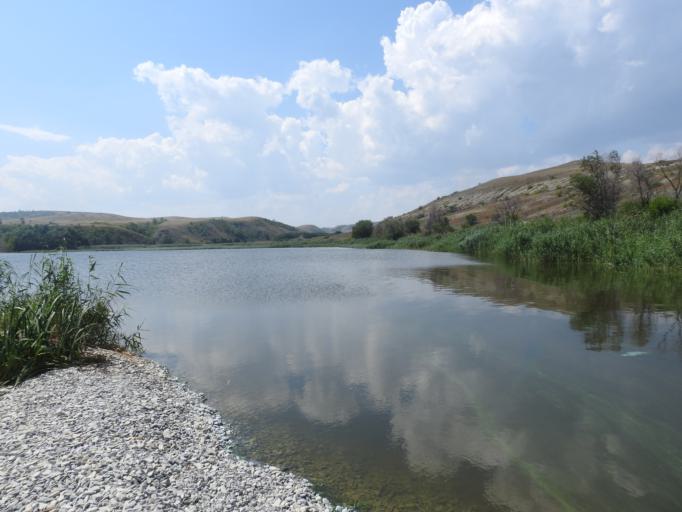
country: RU
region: Saratov
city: Kamenskiy
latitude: 50.5810
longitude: 45.7035
